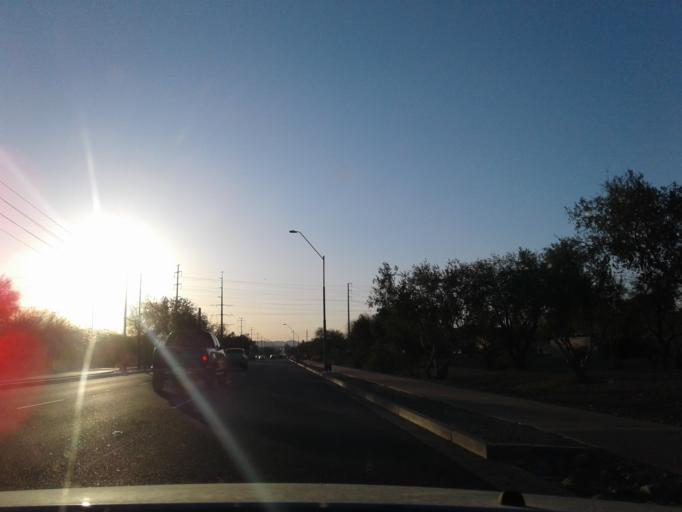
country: US
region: Arizona
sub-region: Maricopa County
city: Scottsdale
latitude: 33.5826
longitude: -111.8262
